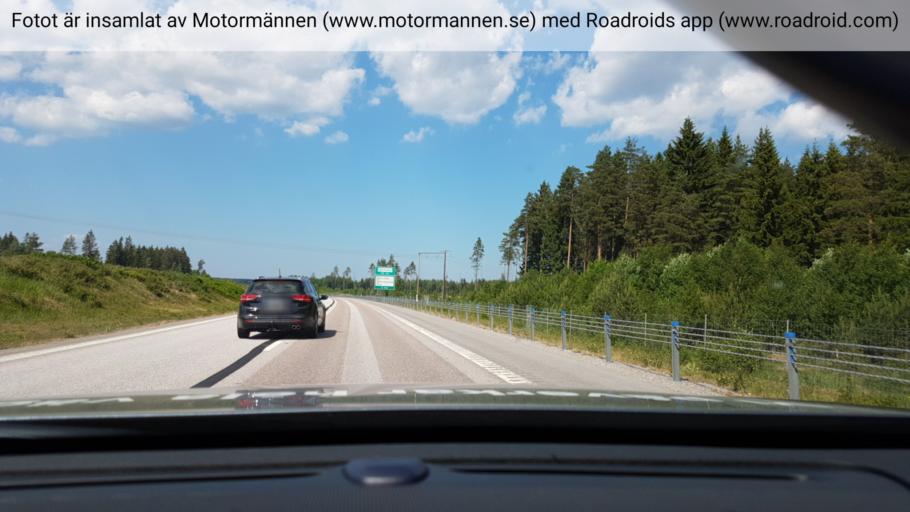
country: SE
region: Uppsala
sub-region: Tierps Kommun
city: Tierp
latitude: 60.3099
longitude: 17.5219
